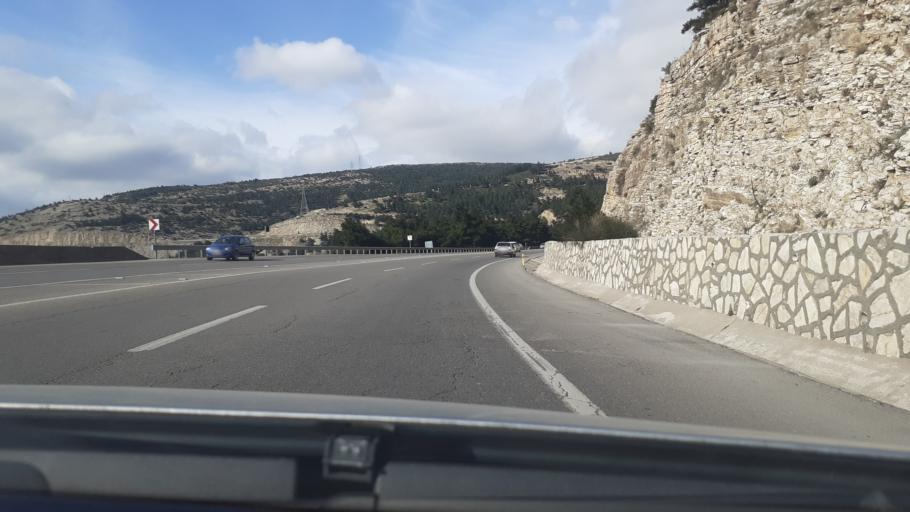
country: TR
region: Hatay
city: Belen
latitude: 36.4759
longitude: 36.2443
